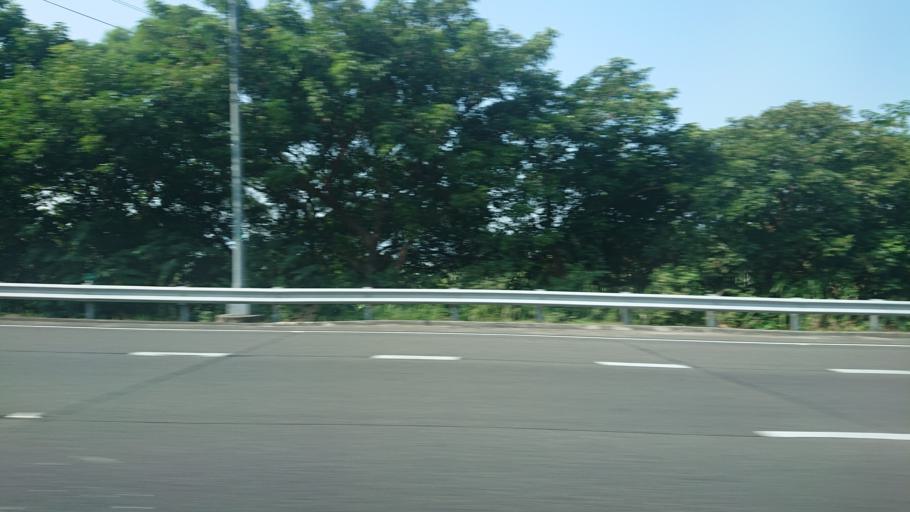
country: TW
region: Taiwan
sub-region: Nantou
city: Nantou
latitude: 23.8457
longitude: 120.7047
